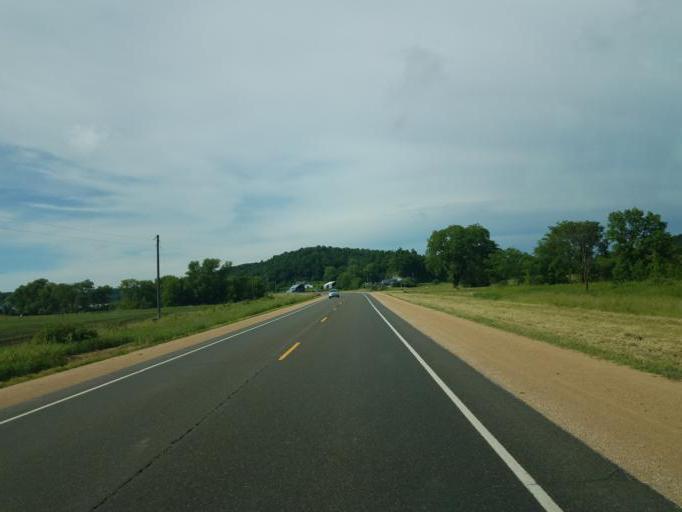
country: US
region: Wisconsin
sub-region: Monroe County
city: Tomah
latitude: 43.8656
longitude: -90.4739
